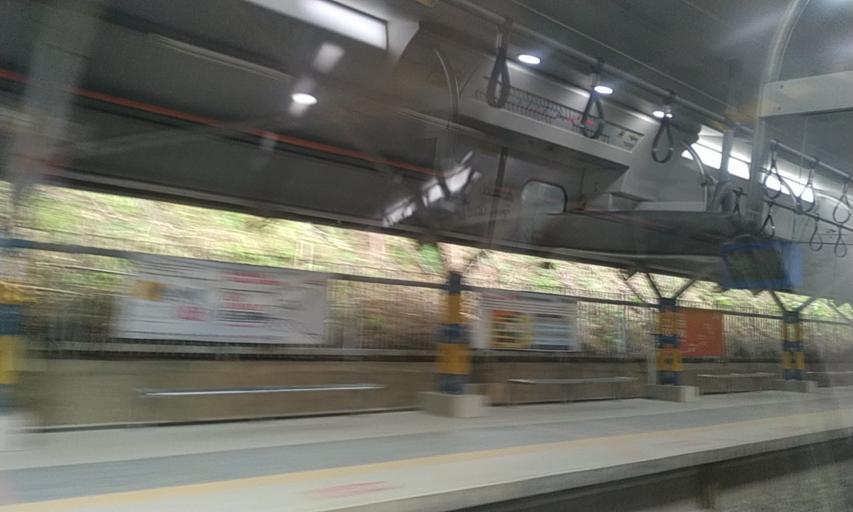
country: MY
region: Kuala Lumpur
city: Kuala Lumpur
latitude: 3.1546
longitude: 101.6930
